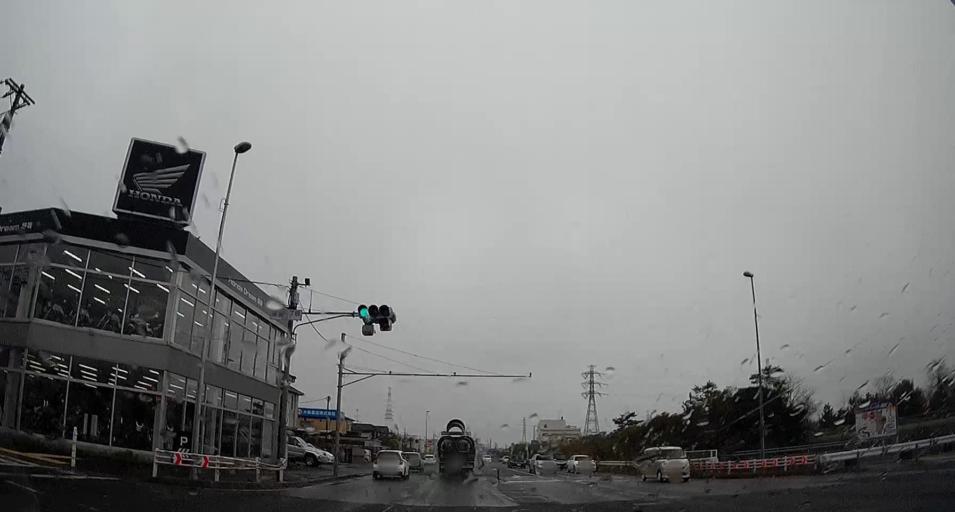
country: JP
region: Chiba
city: Chiba
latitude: 35.5728
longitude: 140.1287
